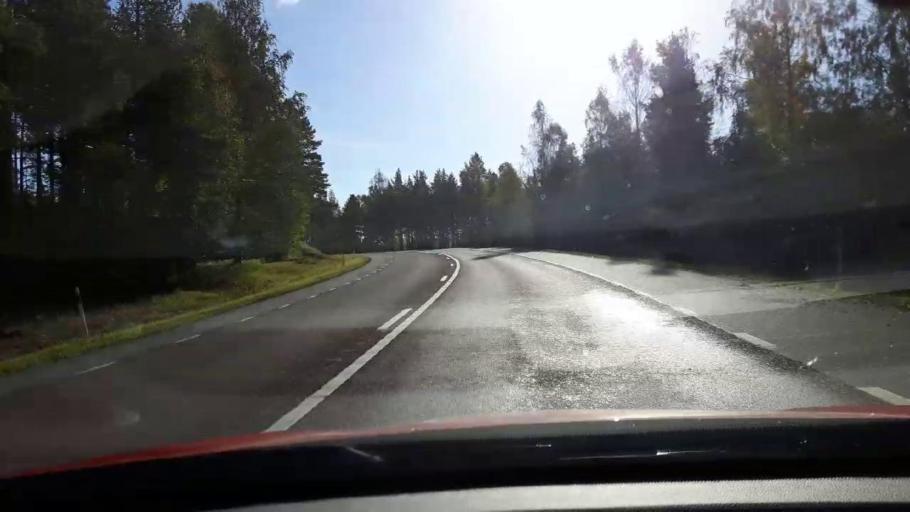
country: SE
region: Jaemtland
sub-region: OEstersunds Kommun
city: Brunflo
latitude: 62.9433
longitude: 15.0745
